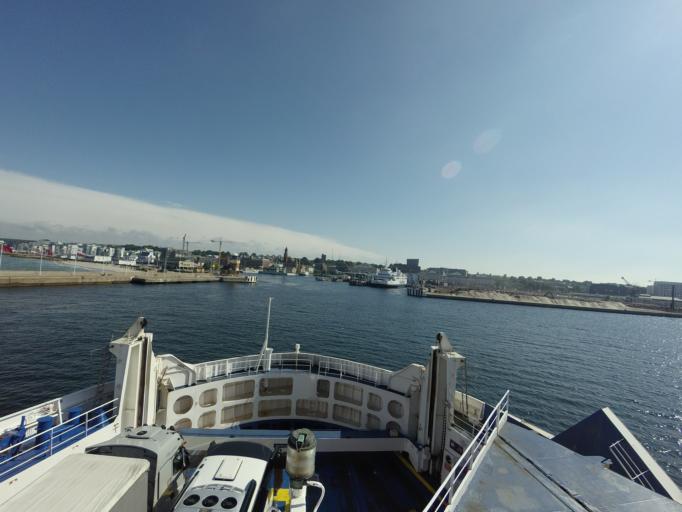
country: SE
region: Skane
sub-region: Helsingborg
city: Helsingborg
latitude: 56.0413
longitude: 12.6861
